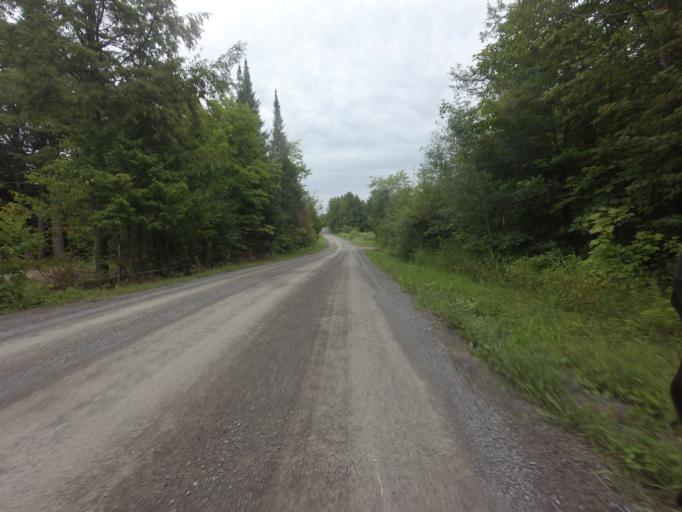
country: CA
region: Ontario
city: Carleton Place
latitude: 45.1536
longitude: -76.2602
